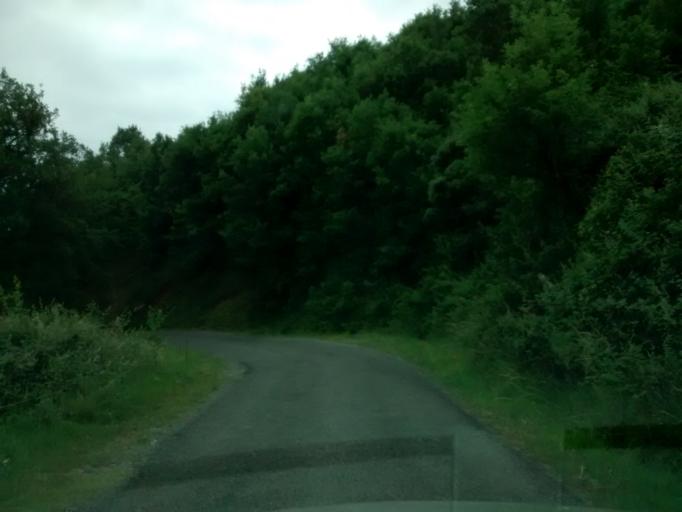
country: ES
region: Aragon
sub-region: Provincia de Huesca
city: Puertolas
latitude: 42.5413
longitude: 0.1332
